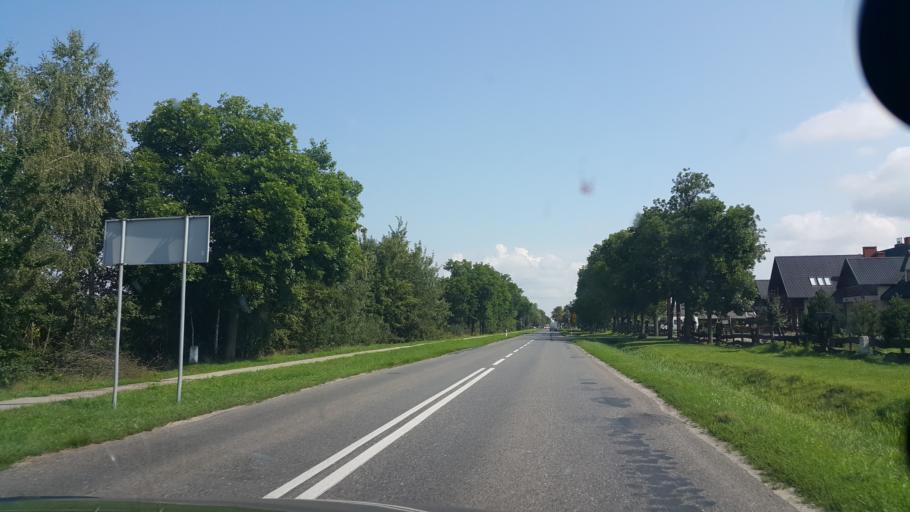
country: PL
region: Lublin Voivodeship
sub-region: Powiat wlodawski
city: Urszulin
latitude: 51.3881
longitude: 23.1915
